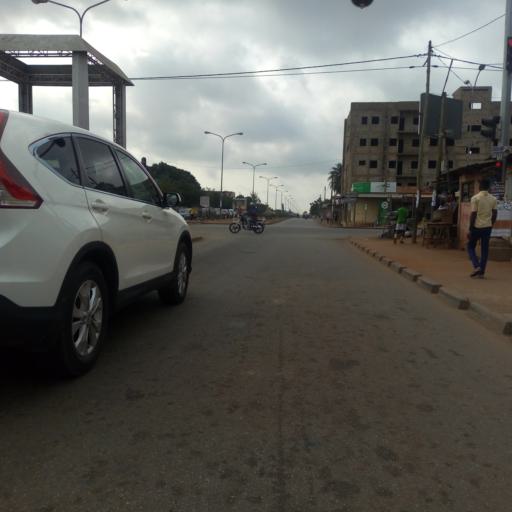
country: TG
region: Maritime
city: Lome
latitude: 6.1925
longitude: 1.2444
